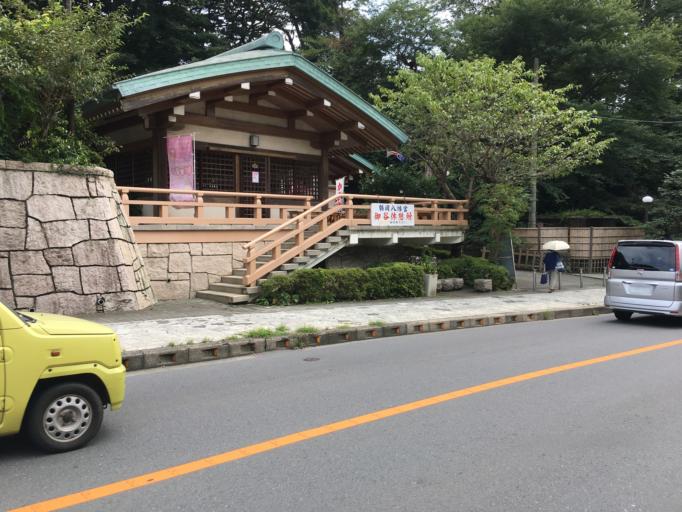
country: JP
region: Kanagawa
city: Kamakura
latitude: 35.3269
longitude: 139.5560
